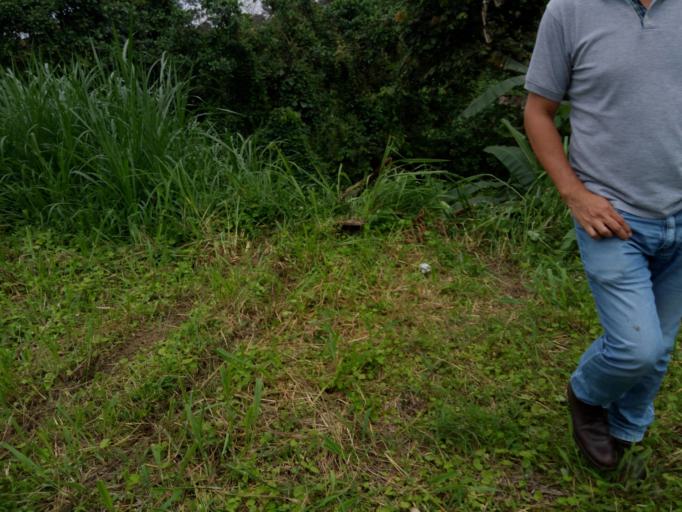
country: EC
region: Santo Domingo de los Tsachilas
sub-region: Canton Santo Domingo de los Colorados
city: Santo Domingo de los Colorados
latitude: -0.2282
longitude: -79.2066
